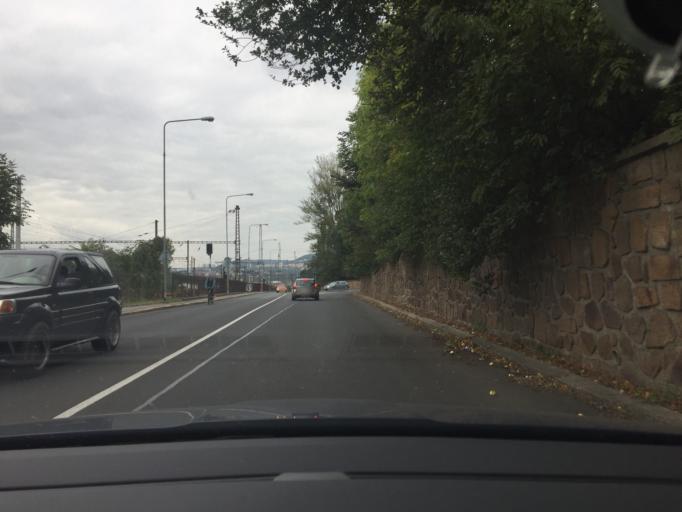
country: CZ
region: Ustecky
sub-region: Okres Usti nad Labem
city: Usti nad Labem
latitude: 50.6436
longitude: 14.0486
